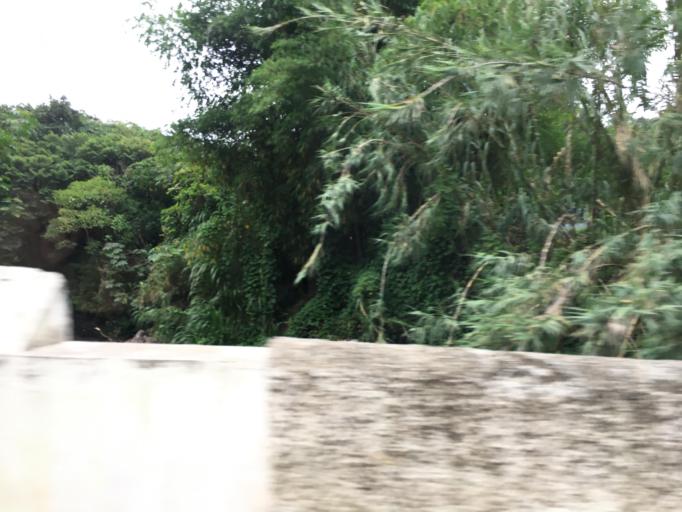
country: GT
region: Sacatepequez
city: Pastores
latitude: 14.5970
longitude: -90.7555
